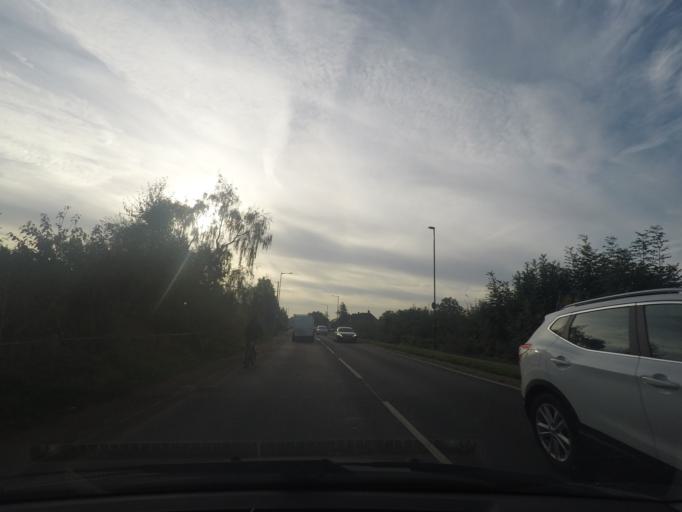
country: GB
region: England
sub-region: City of York
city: Fulford
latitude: 53.9297
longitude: -1.0708
